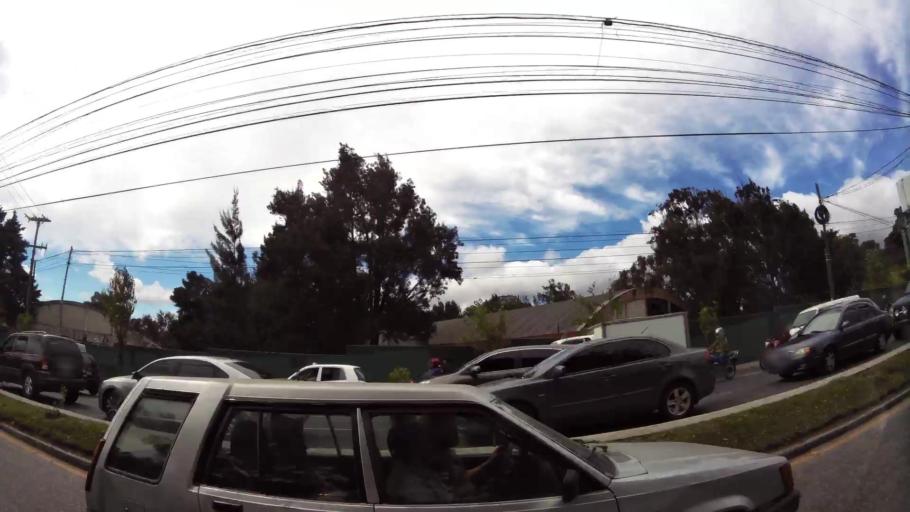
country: GT
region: Guatemala
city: Guatemala City
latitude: 14.5991
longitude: -90.5308
